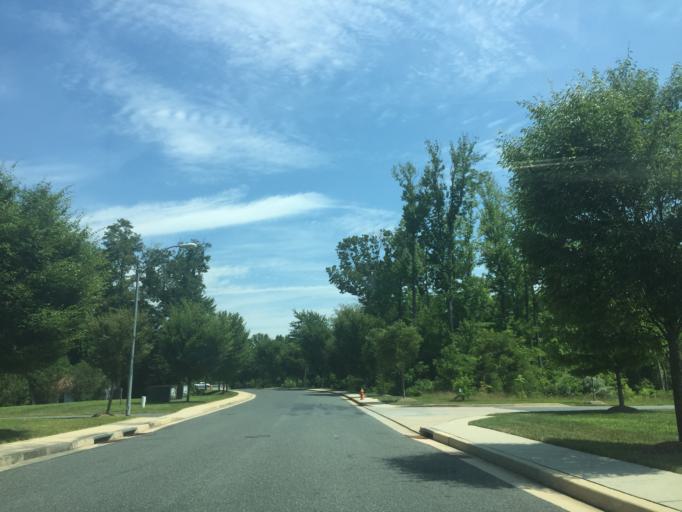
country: US
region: Maryland
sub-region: Baltimore County
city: Middle River
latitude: 39.3429
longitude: -76.4182
